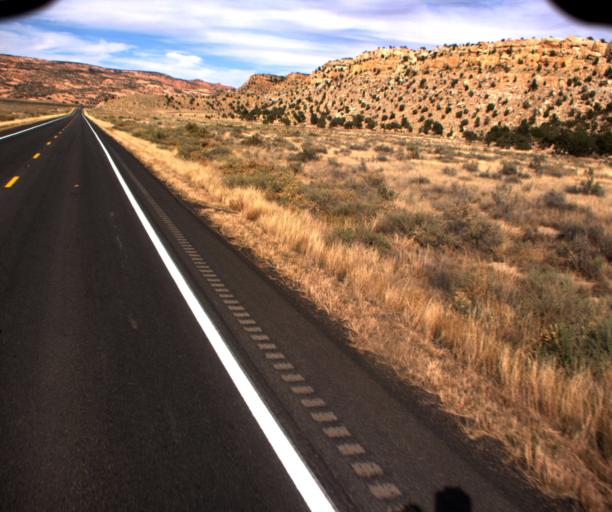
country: US
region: Arizona
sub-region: Navajo County
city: Kayenta
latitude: 36.5990
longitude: -110.4725
